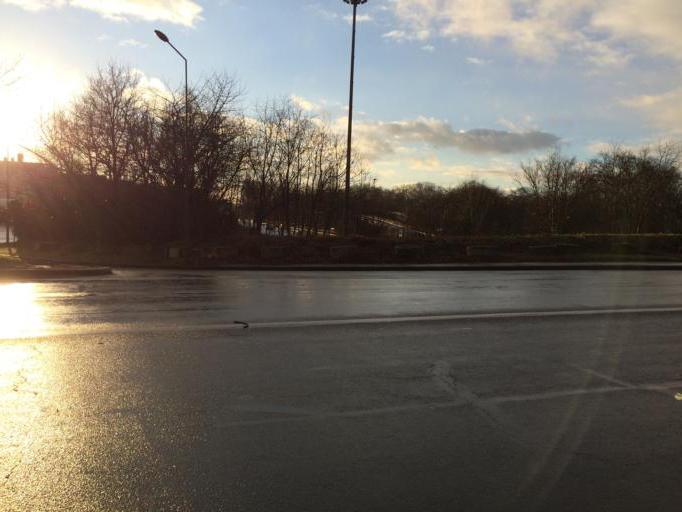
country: FR
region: Ile-de-France
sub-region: Departement du Val-de-Marne
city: Orly
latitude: 48.7547
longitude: 2.3861
